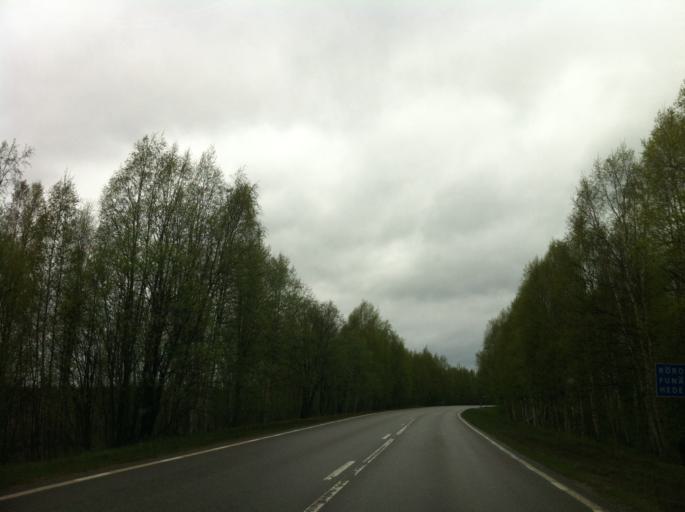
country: SE
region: Jaemtland
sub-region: Harjedalens Kommun
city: Sveg
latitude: 62.1286
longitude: 14.0641
